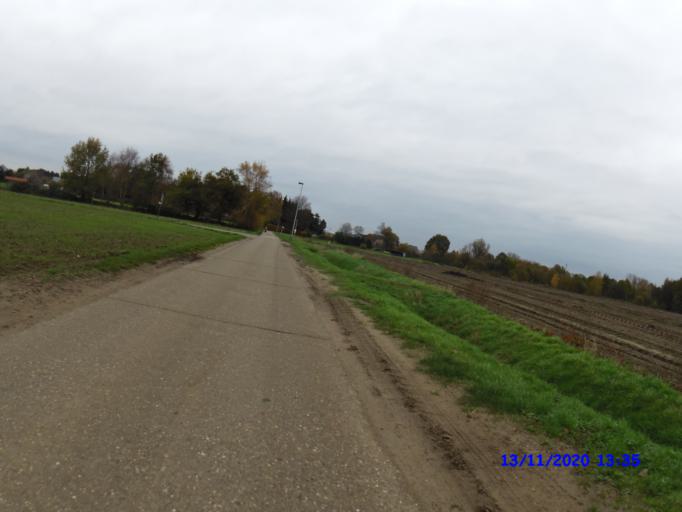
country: BE
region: Flanders
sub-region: Provincie Antwerpen
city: Kasterlee
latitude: 51.2425
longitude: 5.0022
